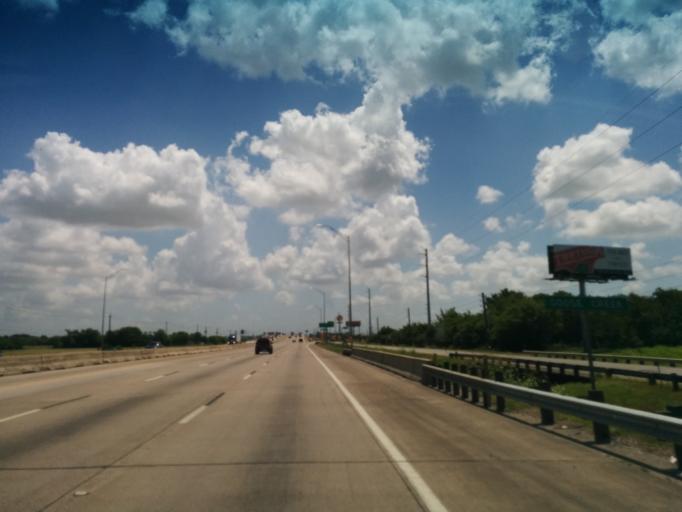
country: US
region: Texas
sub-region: Harris County
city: Highlands
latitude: 29.8009
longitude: -95.0049
